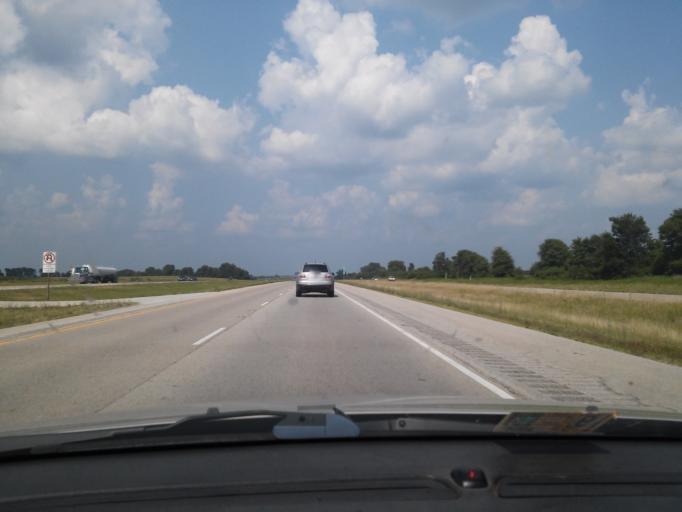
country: US
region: Illinois
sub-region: McLean County
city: Lexington
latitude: 40.5937
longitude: -88.8550
